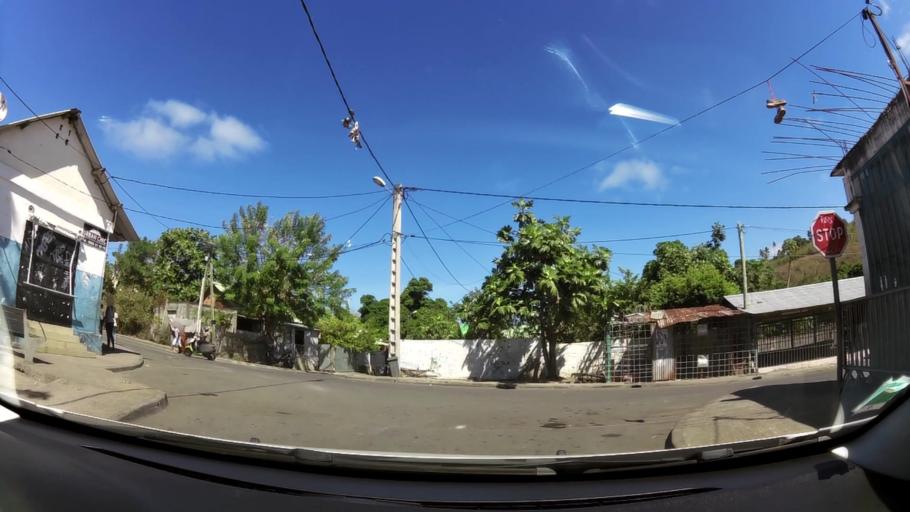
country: YT
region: Pamandzi
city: Pamandzi
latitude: -12.7890
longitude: 45.2795
